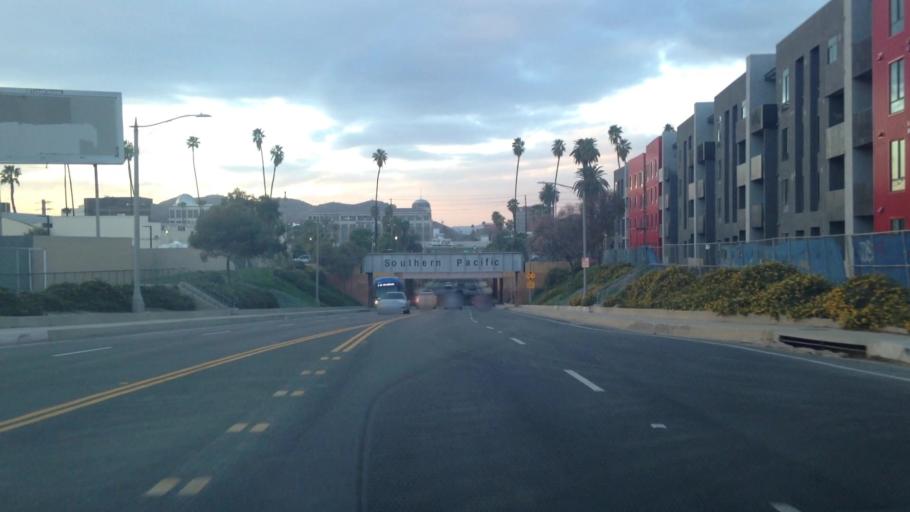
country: US
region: California
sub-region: Riverside County
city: Riverside
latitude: 33.9778
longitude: -117.3655
